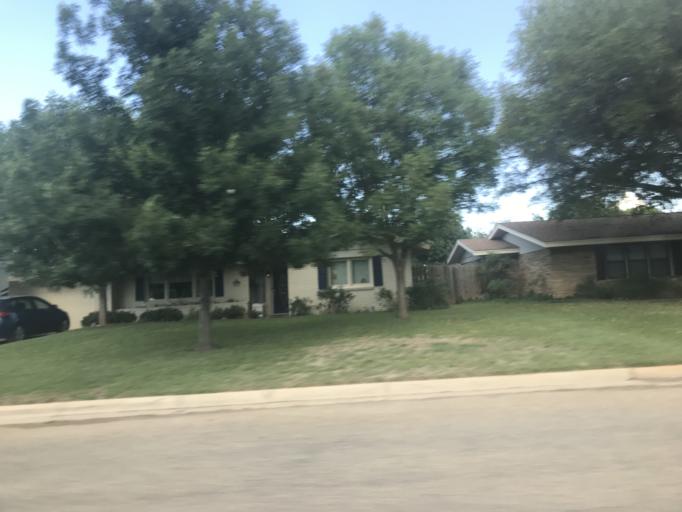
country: US
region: Texas
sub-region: Taylor County
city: Abilene
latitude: 32.4282
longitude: -99.7670
